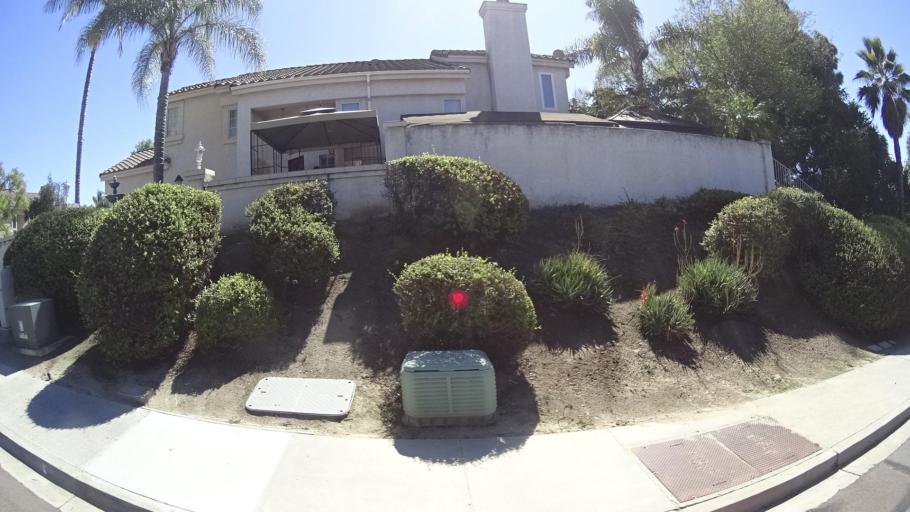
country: US
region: California
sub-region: San Diego County
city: Bonita
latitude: 32.6423
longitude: -117.0474
